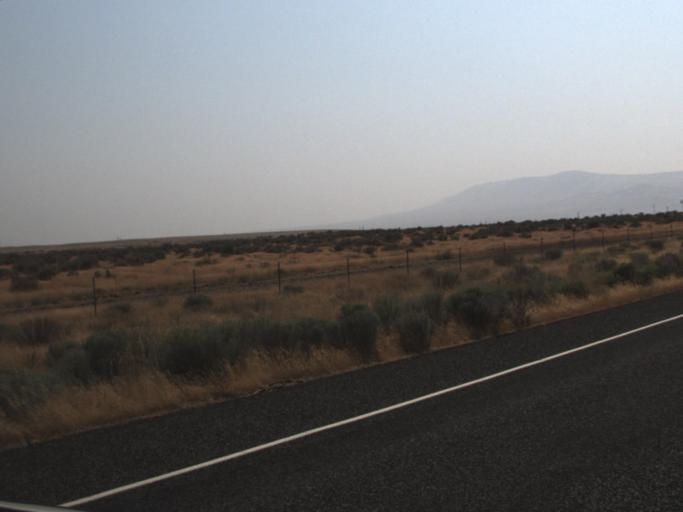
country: US
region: Washington
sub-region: Grant County
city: Desert Aire
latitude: 46.5821
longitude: -119.7281
